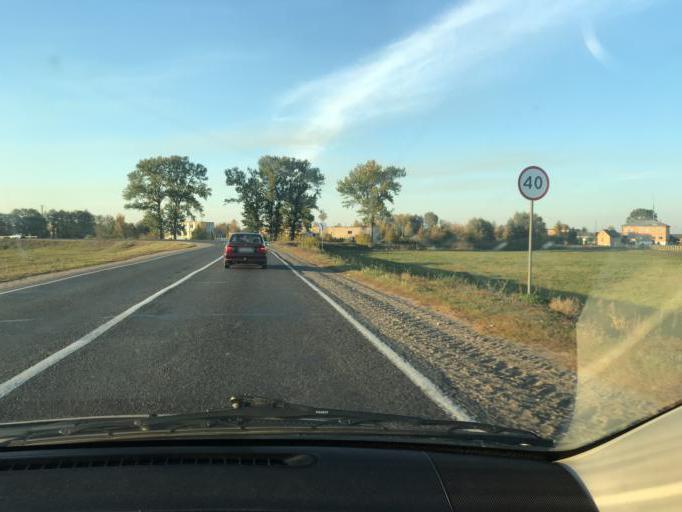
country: BY
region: Brest
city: Pinsk
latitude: 52.0630
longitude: 26.2091
